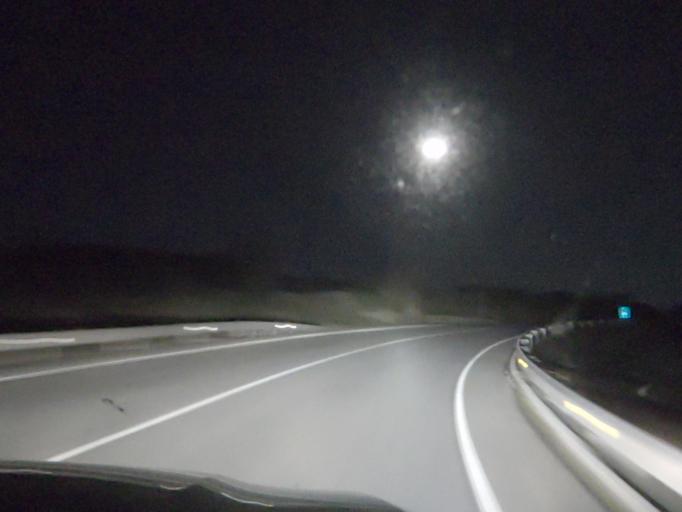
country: ES
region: Galicia
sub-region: Provincia de Ourense
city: Cualedro
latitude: 41.9811
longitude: -7.5318
